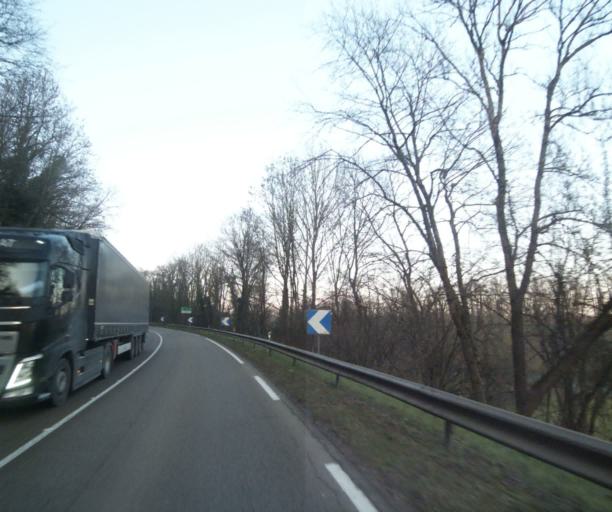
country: FR
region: Champagne-Ardenne
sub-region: Departement de la Haute-Marne
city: Bienville
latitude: 48.6001
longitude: 5.0334
